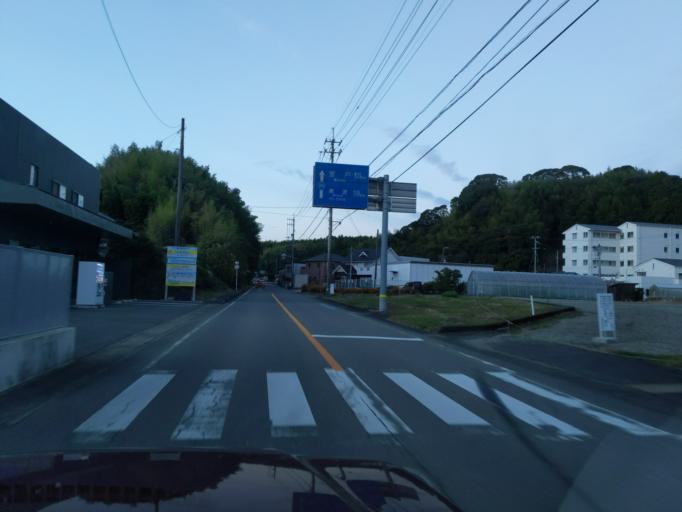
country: JP
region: Tokushima
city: Anan
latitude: 33.8416
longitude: 134.6230
